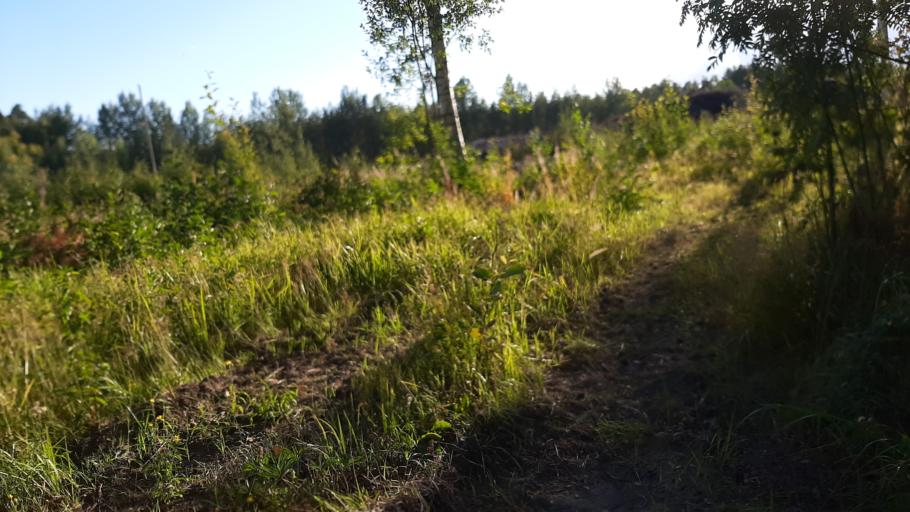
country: FI
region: North Karelia
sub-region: Joensuu
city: Joensuu
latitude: 62.6259
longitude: 29.7530
